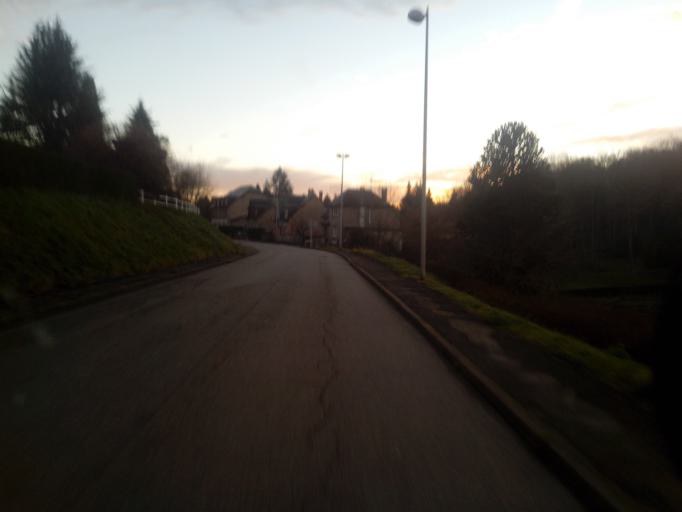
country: FR
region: Limousin
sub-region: Departement de la Correze
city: Meymac
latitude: 45.5393
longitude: 2.1414
